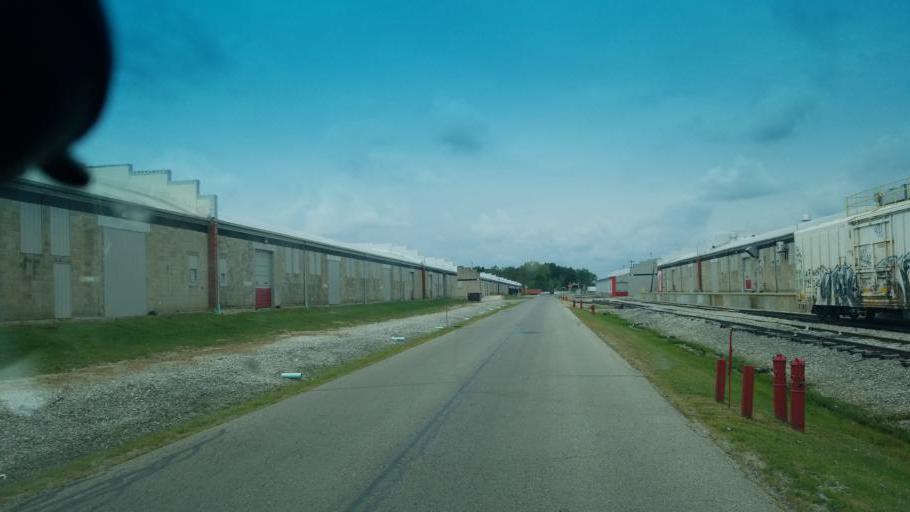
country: US
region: Ohio
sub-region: Richland County
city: Shelby
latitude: 40.9003
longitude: -82.6701
